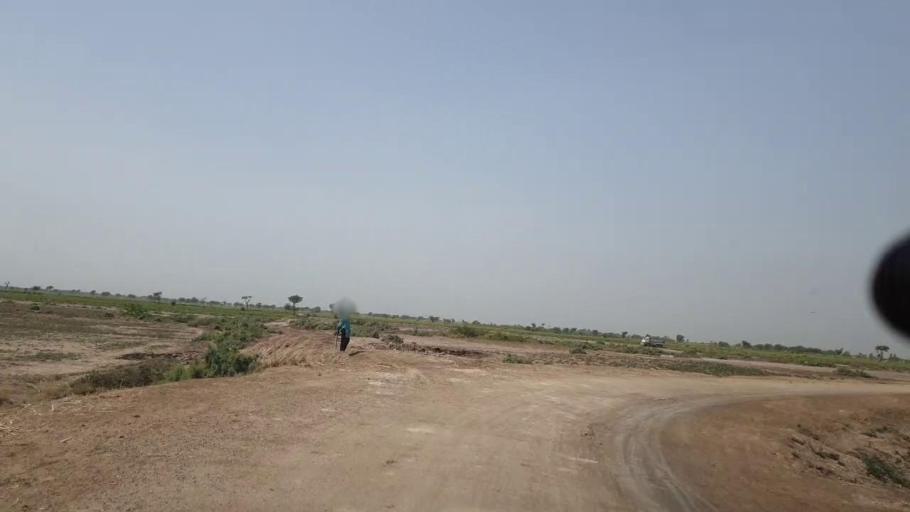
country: PK
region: Sindh
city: Matli
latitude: 25.0677
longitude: 68.6911
